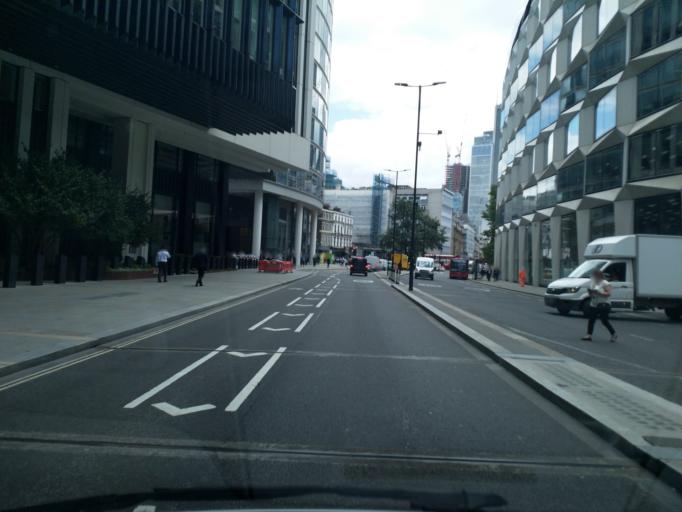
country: GB
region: England
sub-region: Greater London
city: Barbican
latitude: 51.5175
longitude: -0.0913
